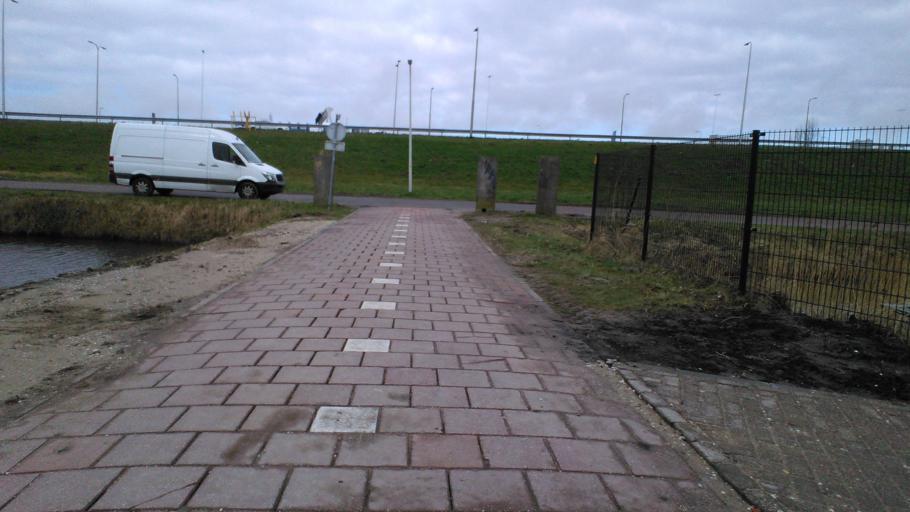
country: NL
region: South Holland
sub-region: Gemeente Den Haag
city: Ypenburg
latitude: 52.0579
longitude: 4.3730
